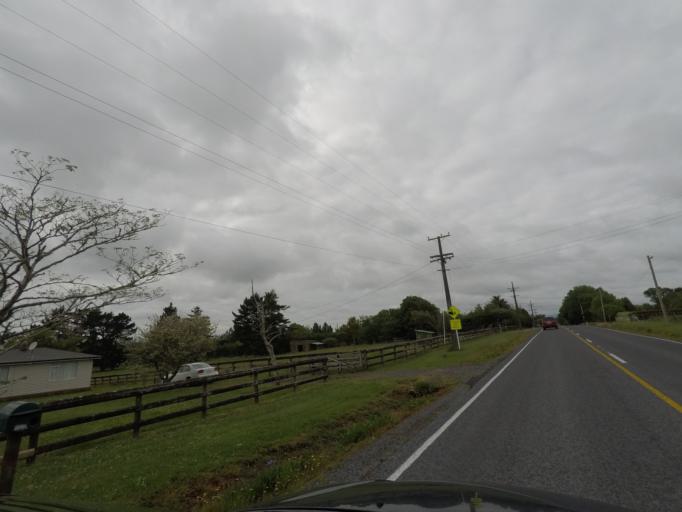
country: NZ
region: Auckland
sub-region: Auckland
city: Rosebank
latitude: -36.7949
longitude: 174.5741
